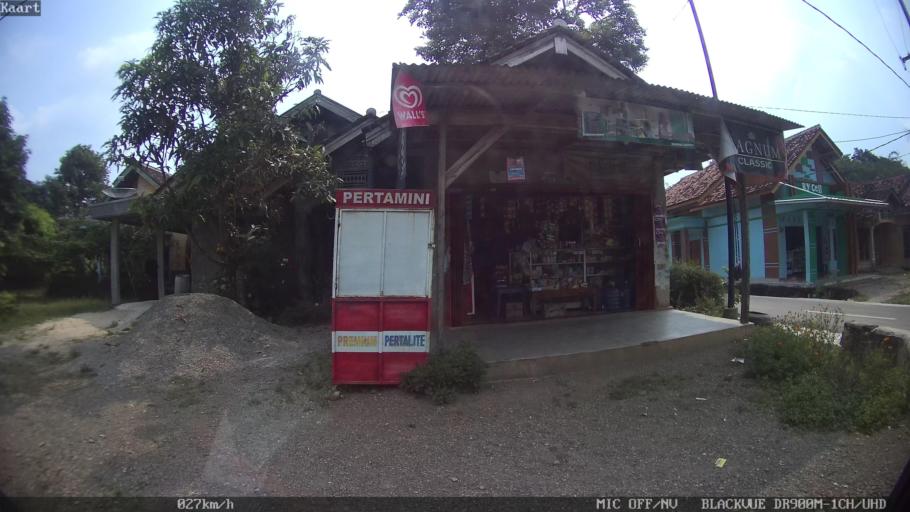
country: ID
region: Lampung
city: Gadingrejo
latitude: -5.3600
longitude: 105.0418
